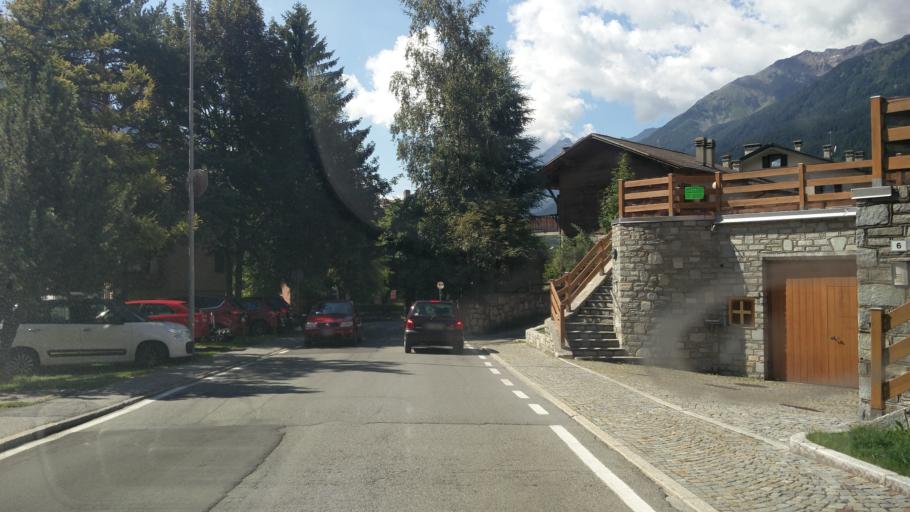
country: IT
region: Lombardy
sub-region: Provincia di Sondrio
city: Bormio
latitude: 46.4668
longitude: 10.3669
